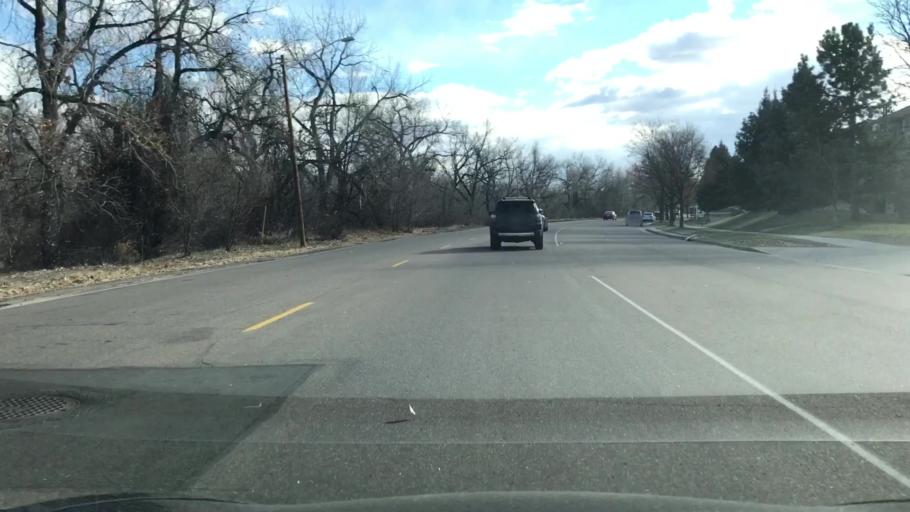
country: US
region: Colorado
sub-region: Arapahoe County
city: Glendale
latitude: 39.7024
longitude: -104.9294
